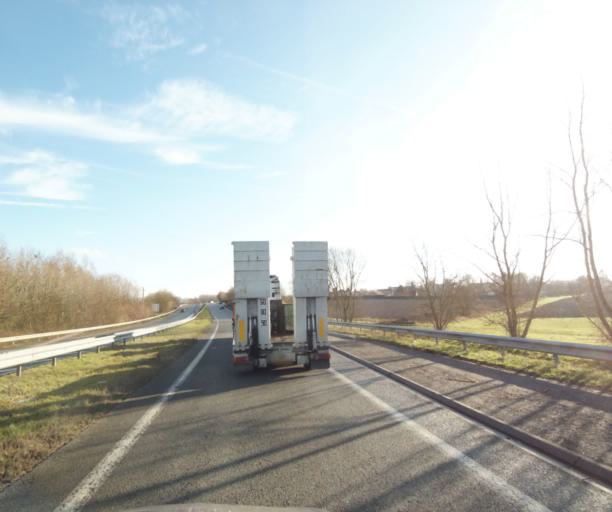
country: FR
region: Nord-Pas-de-Calais
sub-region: Departement du Nord
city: Saultain
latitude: 50.3464
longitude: 3.5766
